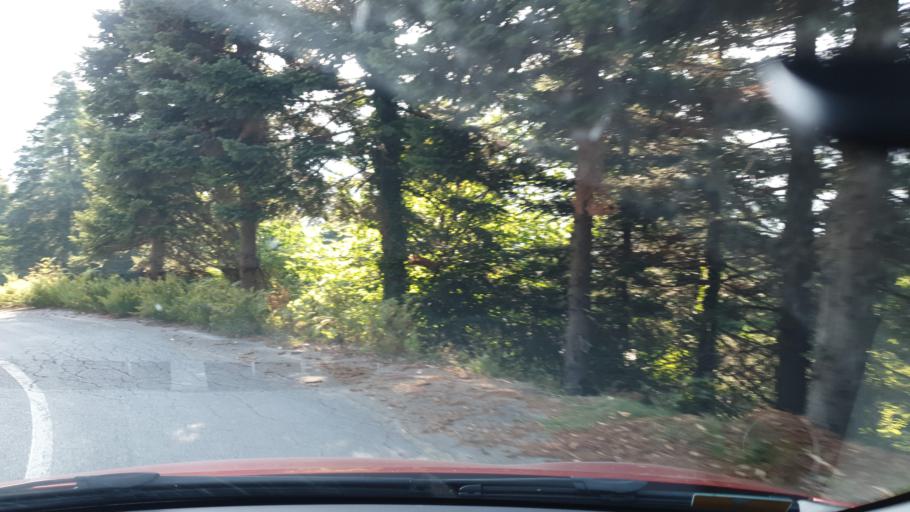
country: GR
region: Central Greece
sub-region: Nomos Evvoias
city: Yimnon
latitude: 38.5995
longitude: 23.9009
